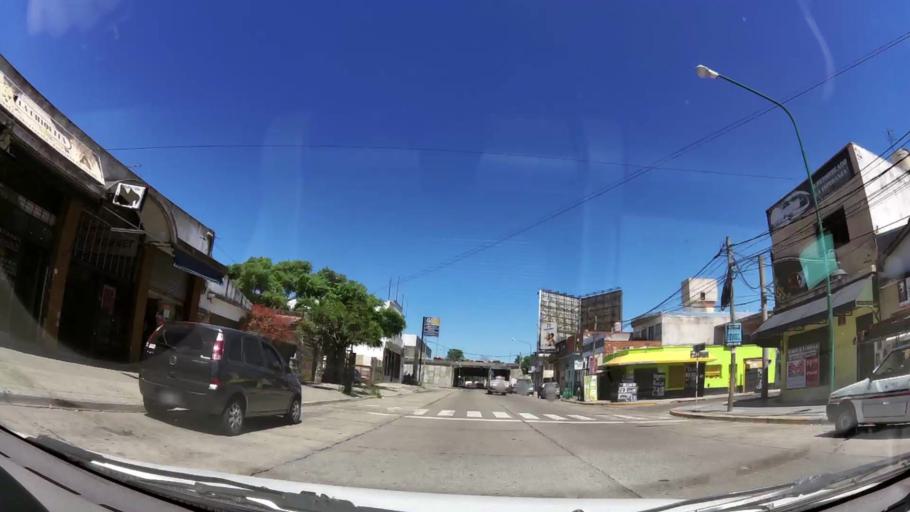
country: AR
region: Buenos Aires
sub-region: Partido de Vicente Lopez
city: Olivos
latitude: -34.5181
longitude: -58.5137
